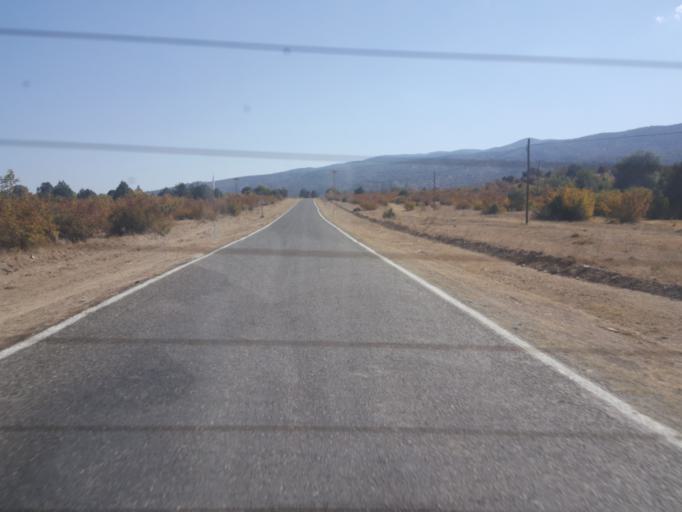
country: TR
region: Kastamonu
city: Tosya
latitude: 41.0014
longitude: 34.1496
